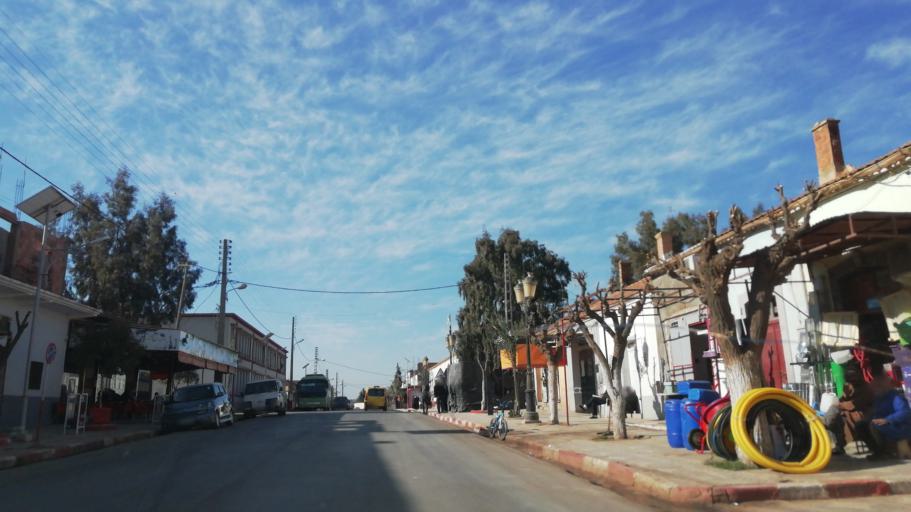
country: DZ
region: Tlemcen
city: Ouled Mimoun
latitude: 35.0253
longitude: -0.8924
